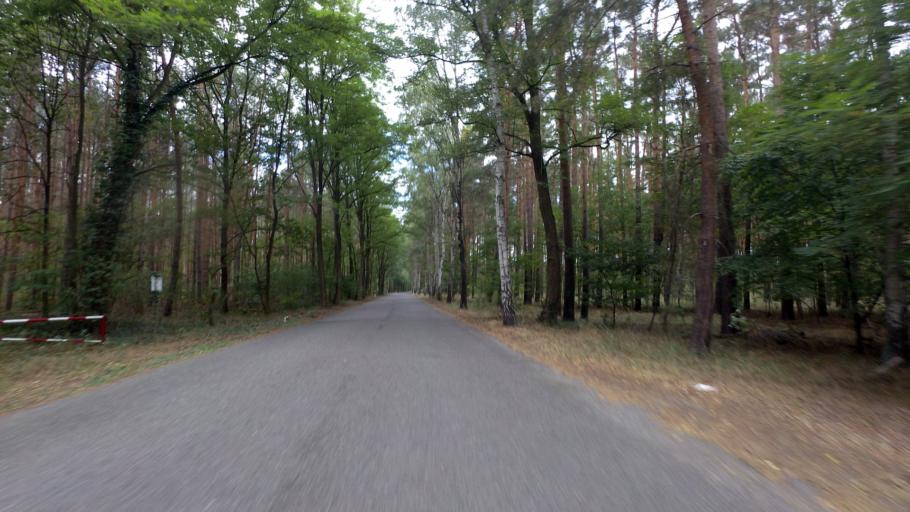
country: DE
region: Brandenburg
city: Spremberg
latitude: 51.6501
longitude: 14.3739
